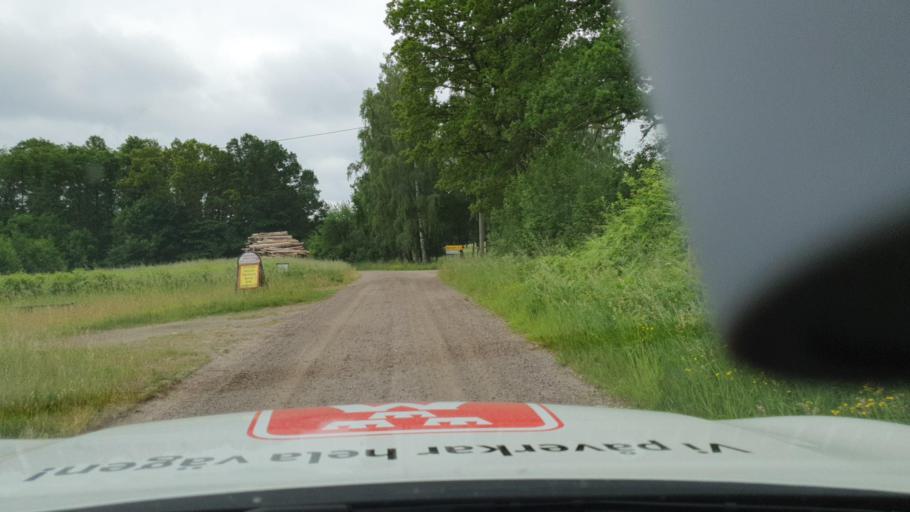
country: SE
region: Vaestra Goetaland
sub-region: Hjo Kommun
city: Hjo
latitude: 58.3585
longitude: 14.3365
